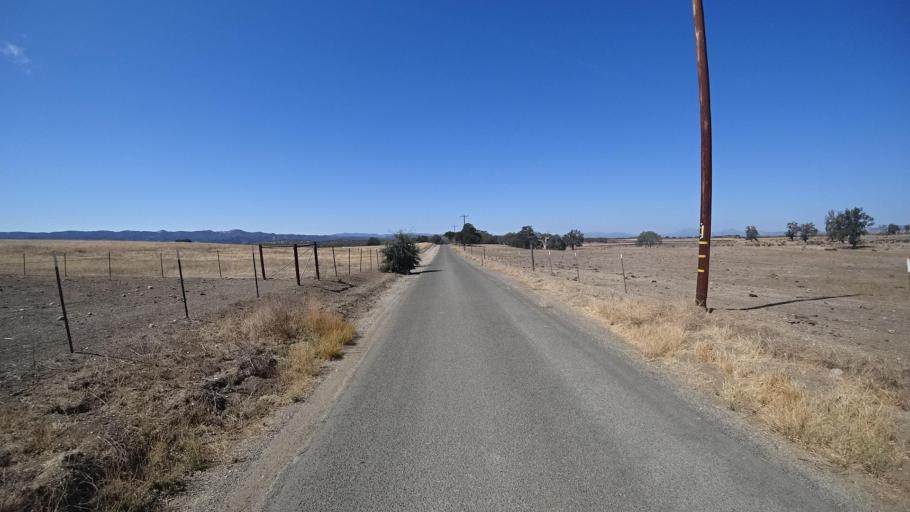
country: US
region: California
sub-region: San Luis Obispo County
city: Lake Nacimiento
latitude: 35.9083
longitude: -121.0336
